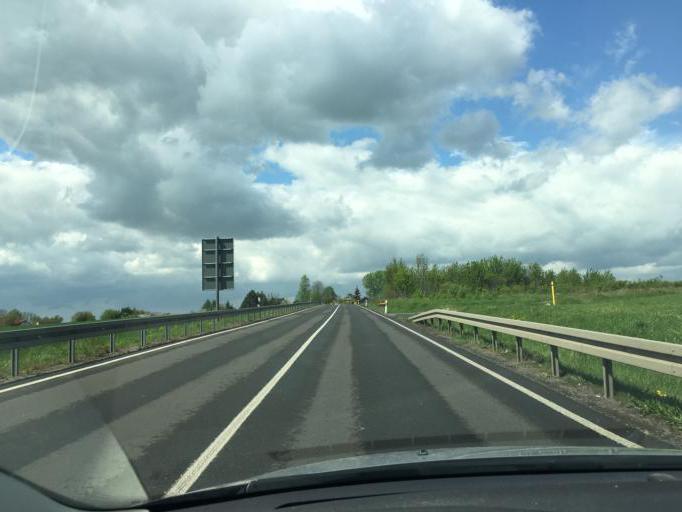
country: DE
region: Saxony
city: Borna
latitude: 51.0985
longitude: 12.5228
